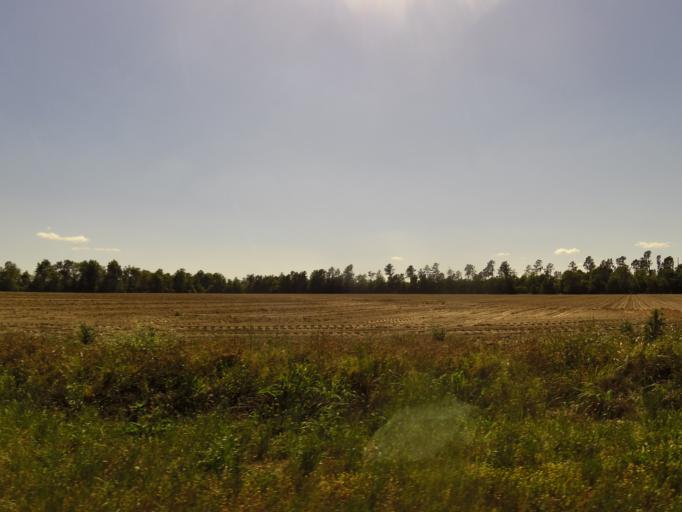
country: US
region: South Carolina
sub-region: Barnwell County
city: Williston
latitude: 33.4413
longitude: -81.4876
